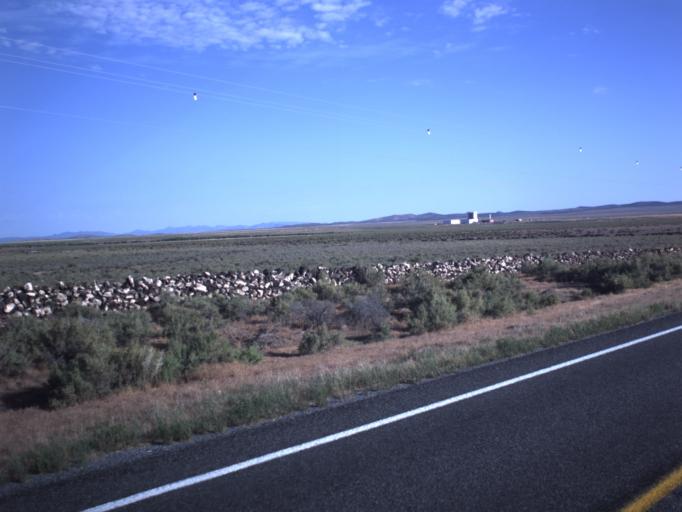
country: US
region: Utah
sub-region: Iron County
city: Enoch
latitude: 37.8598
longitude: -113.0316
